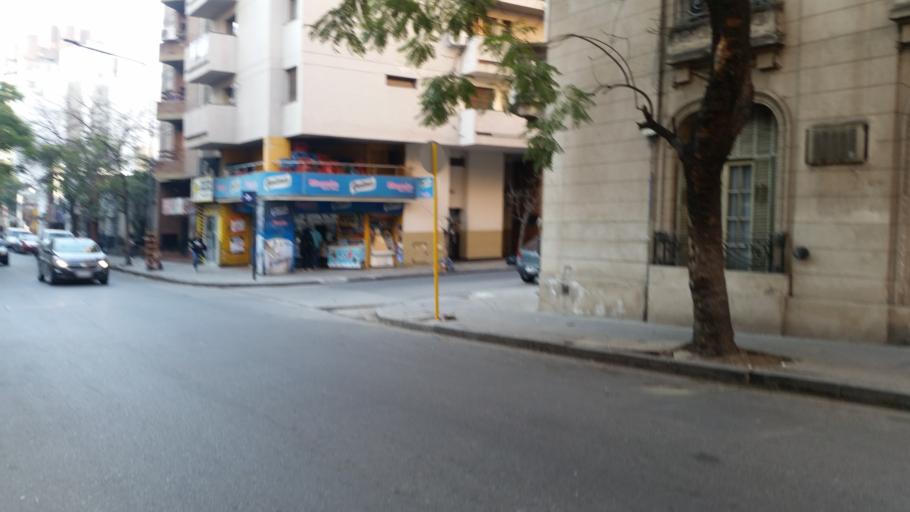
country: AR
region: Cordoba
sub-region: Departamento de Capital
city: Cordoba
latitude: -31.4269
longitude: -64.1886
